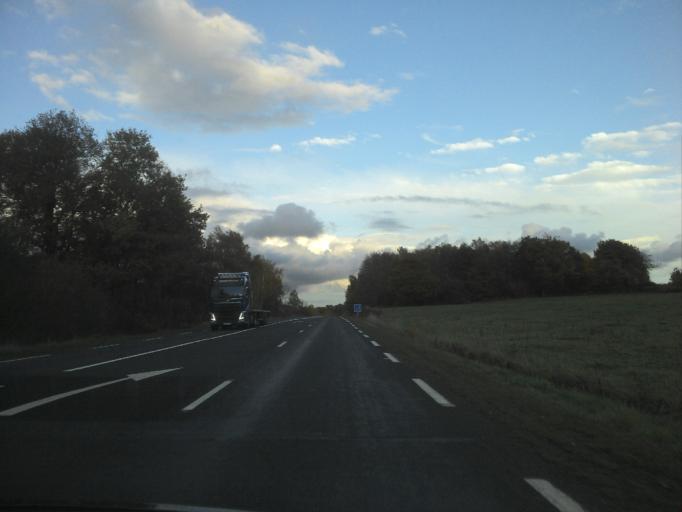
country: FR
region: Auvergne
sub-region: Departement du Puy-de-Dome
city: Gelles
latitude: 45.8435
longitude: 2.7760
